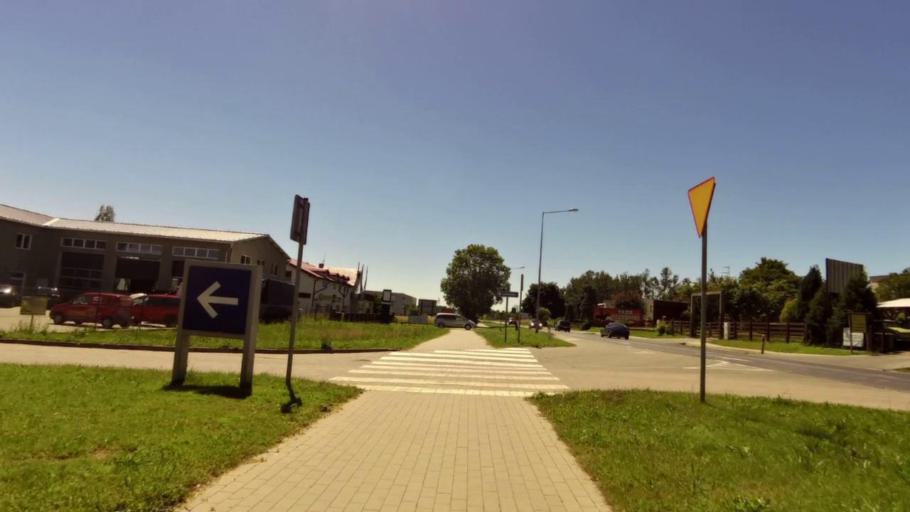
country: PL
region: West Pomeranian Voivodeship
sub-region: Powiat kolobrzeski
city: Kolobrzeg
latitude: 54.1392
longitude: 15.5593
